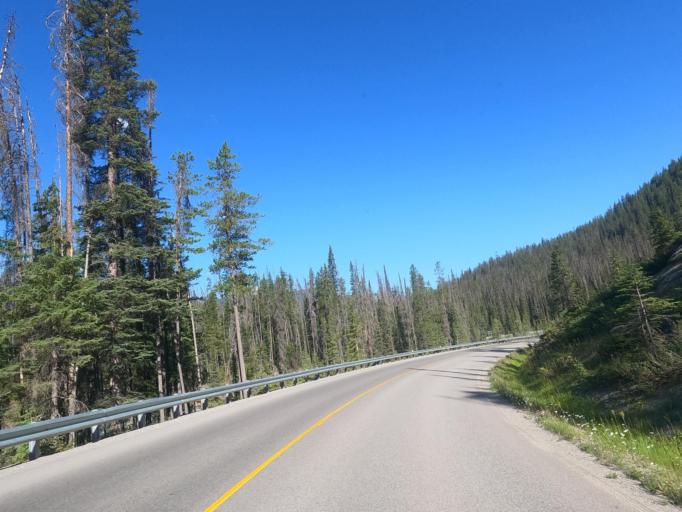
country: CA
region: Alberta
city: Lake Louise
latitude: 51.3817
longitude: -116.5259
